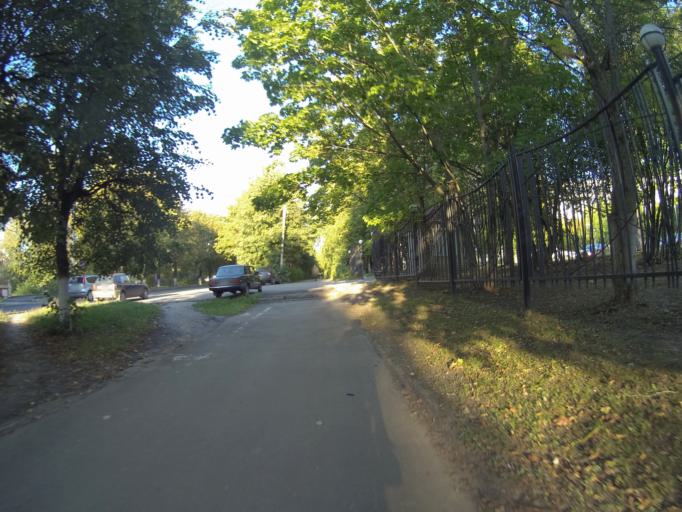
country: RU
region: Vladimir
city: Vladimir
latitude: 56.1467
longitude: 40.3724
